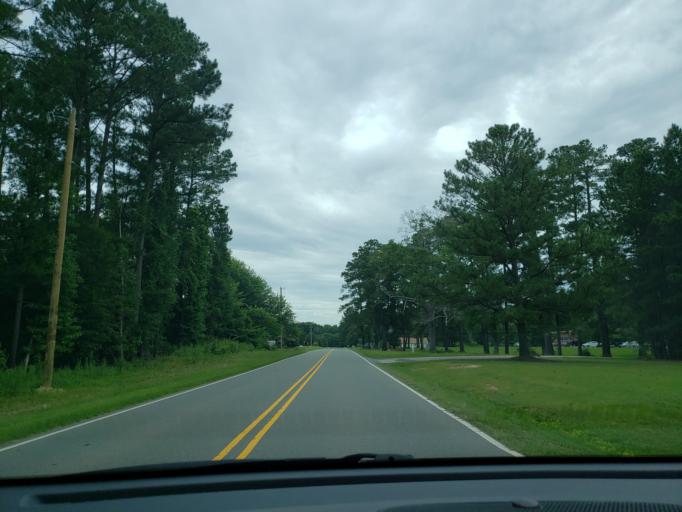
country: US
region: North Carolina
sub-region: Chatham County
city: Fearrington Village
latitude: 35.7538
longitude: -79.0088
